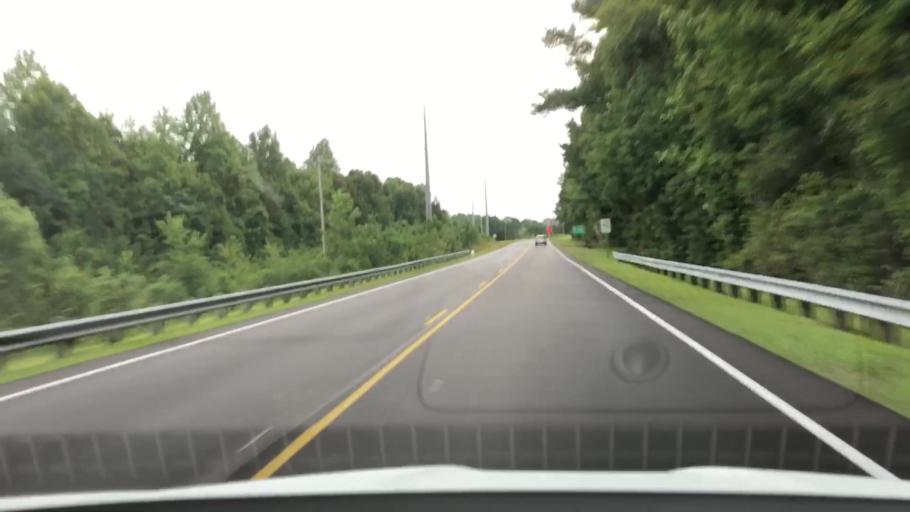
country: US
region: North Carolina
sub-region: Onslow County
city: Swansboro
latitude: 34.7987
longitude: -77.1317
